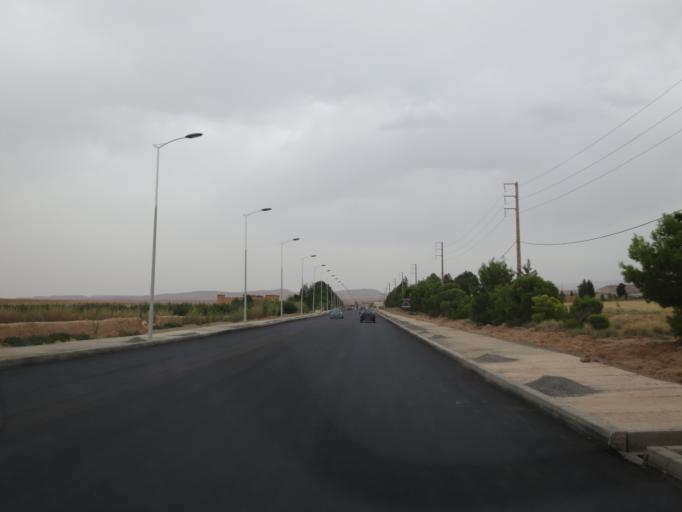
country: MA
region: Meknes-Tafilalet
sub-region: Khenifra
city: Midelt
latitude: 32.7065
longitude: -4.7962
